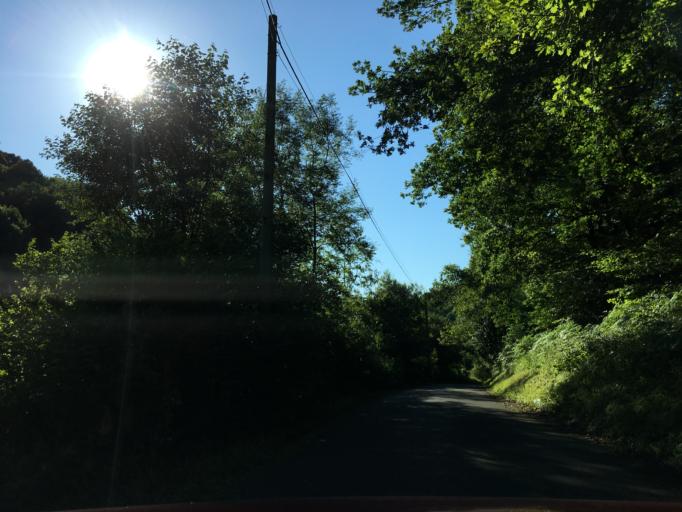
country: GB
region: Wales
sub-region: Monmouthshire
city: Tintern
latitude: 51.6998
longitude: -2.7073
